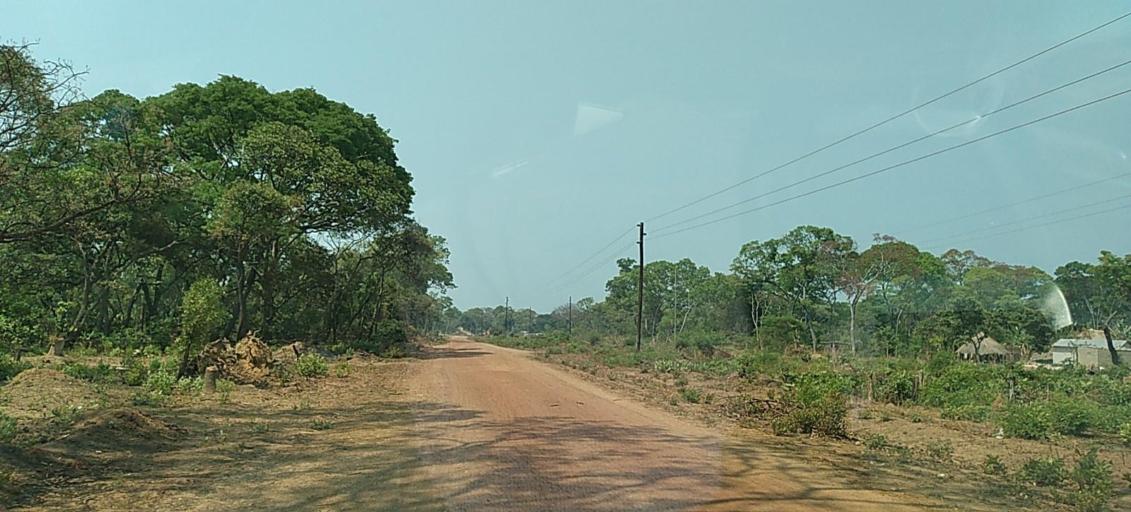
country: ZM
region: Copperbelt
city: Kalulushi
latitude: -13.1043
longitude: 27.4032
